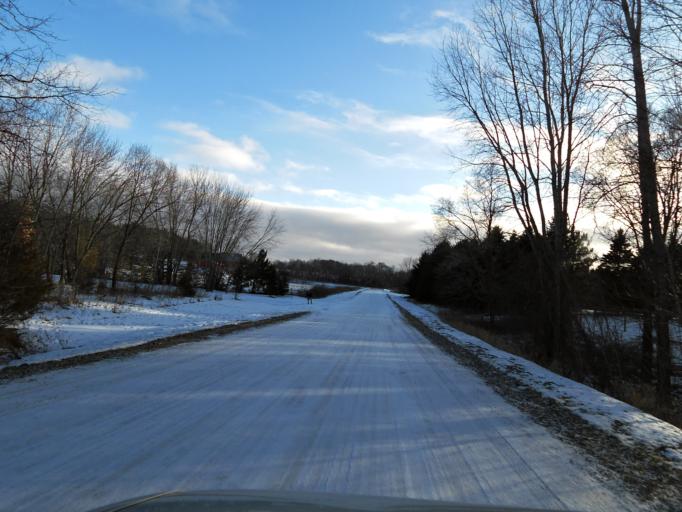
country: US
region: Wisconsin
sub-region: Pierce County
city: Prescott
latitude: 44.7930
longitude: -92.8245
